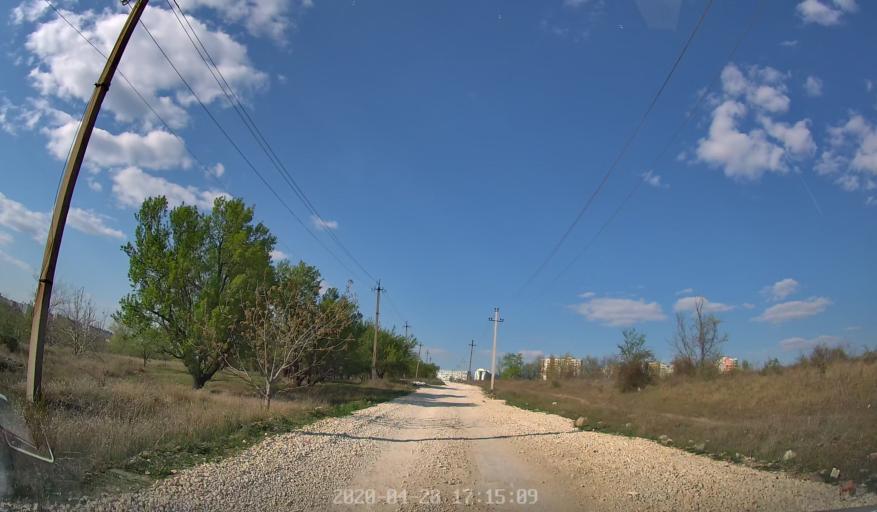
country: MD
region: Chisinau
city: Chisinau
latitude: 46.9692
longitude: 28.8443
